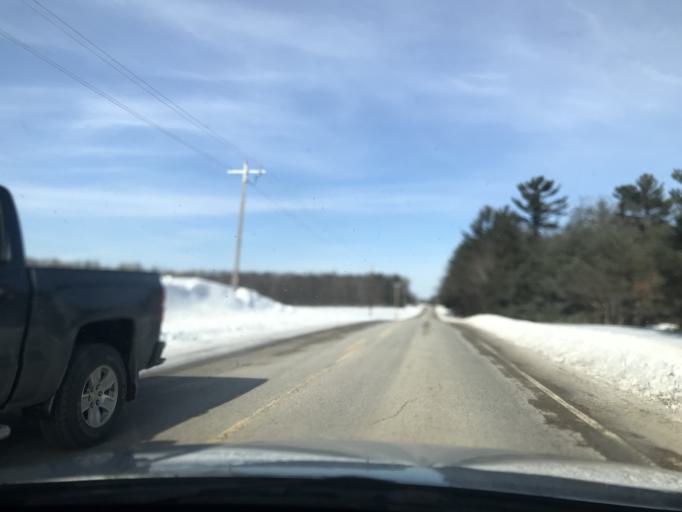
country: US
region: Wisconsin
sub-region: Oconto County
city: Oconto Falls
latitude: 45.1343
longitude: -88.1775
